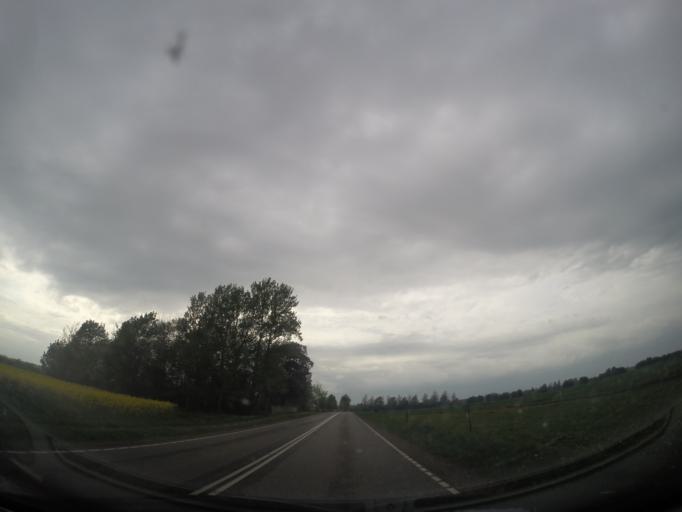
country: DK
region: Capital Region
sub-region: Hoje-Taastrup Kommune
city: Taastrup
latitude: 55.6776
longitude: 12.2658
